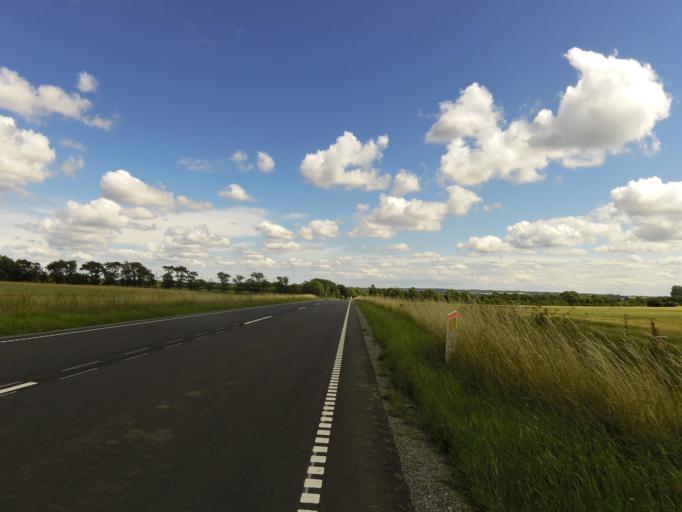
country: DK
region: South Denmark
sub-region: Haderslev Kommune
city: Gram
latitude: 55.3108
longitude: 9.1268
